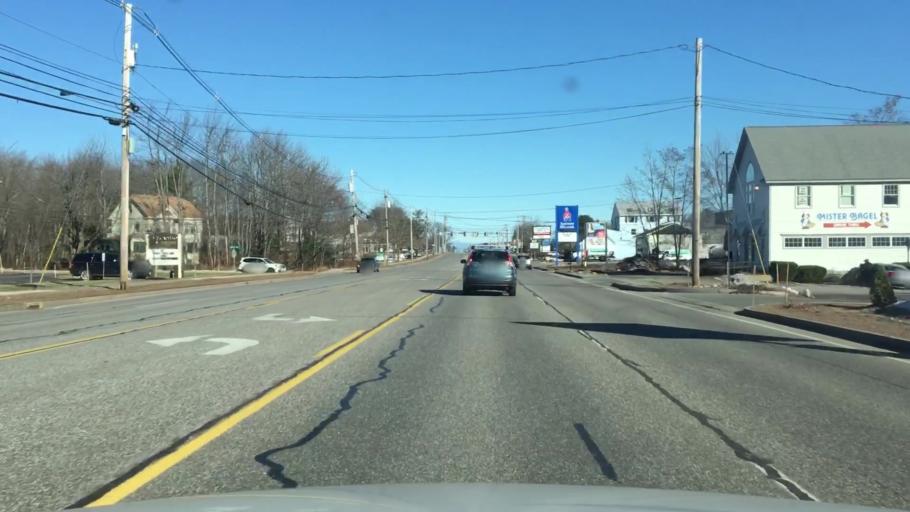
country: US
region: Maine
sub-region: Cumberland County
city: Scarborough
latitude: 43.5953
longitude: -70.3264
